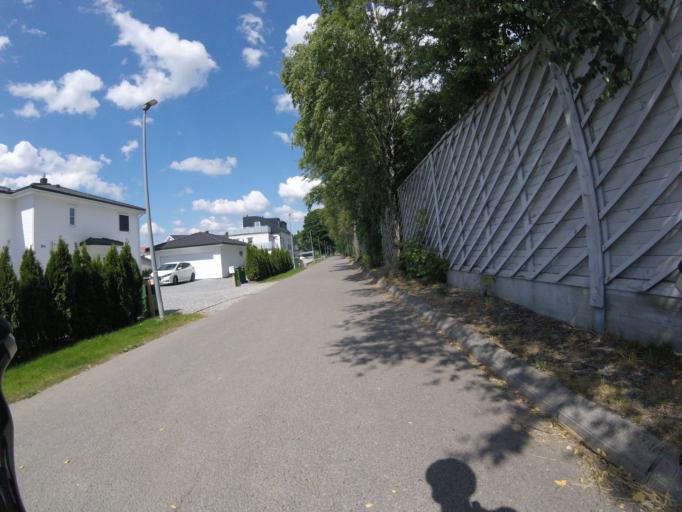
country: NO
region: Akershus
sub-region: Skedsmo
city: Lillestrom
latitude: 59.9571
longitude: 11.0704
